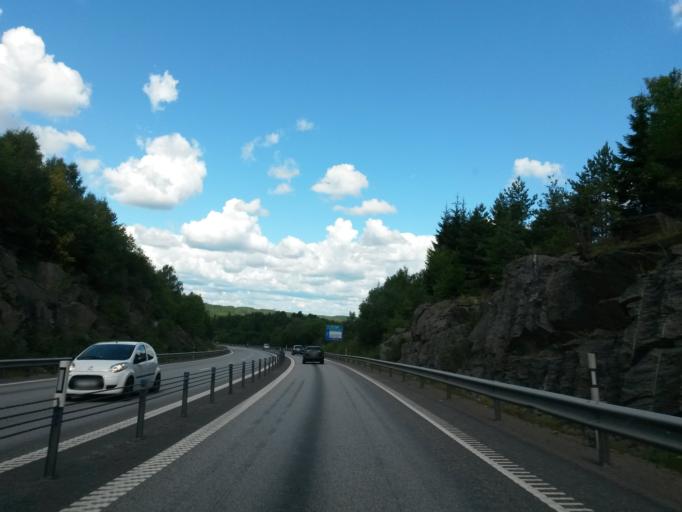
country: SE
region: Vaestra Goetaland
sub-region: Uddevalla Kommun
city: Uddevalla
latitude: 58.3419
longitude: 11.9893
